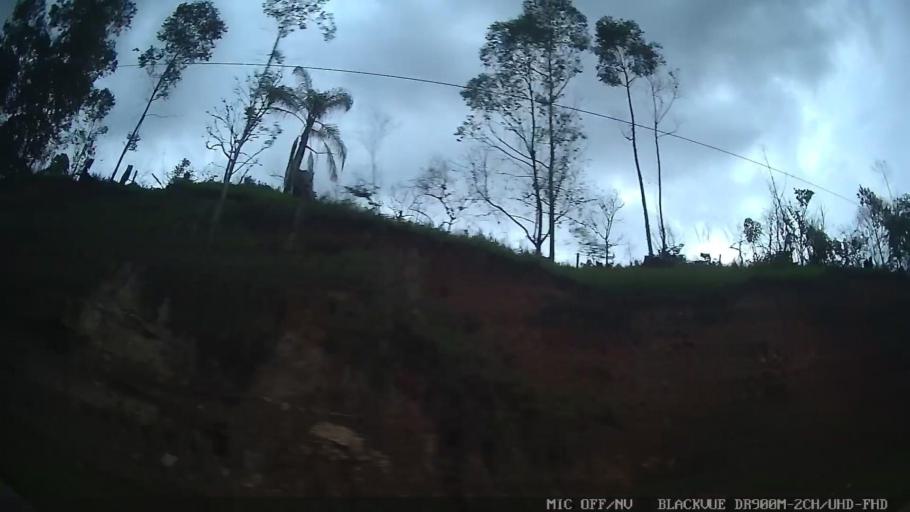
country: BR
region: Sao Paulo
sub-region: Amparo
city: Amparo
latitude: -22.7604
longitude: -46.7554
